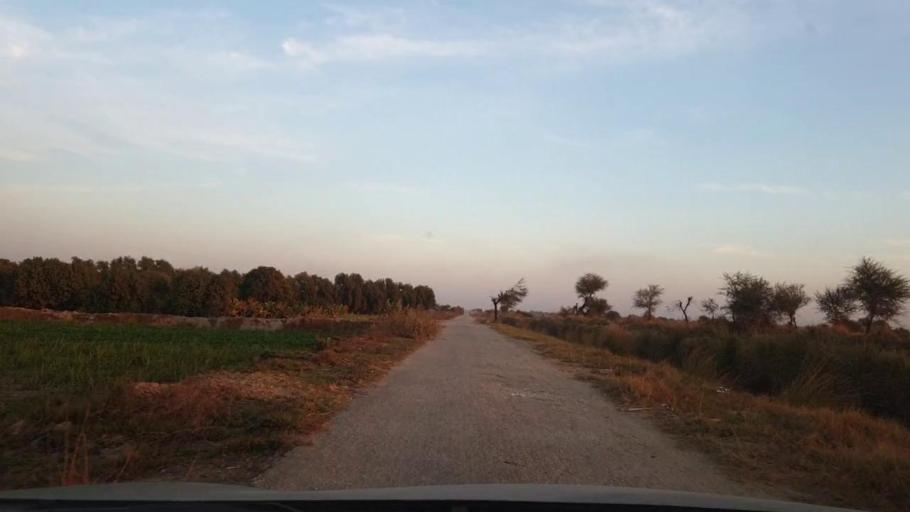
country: PK
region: Sindh
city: Tando Allahyar
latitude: 25.5847
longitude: 68.7211
